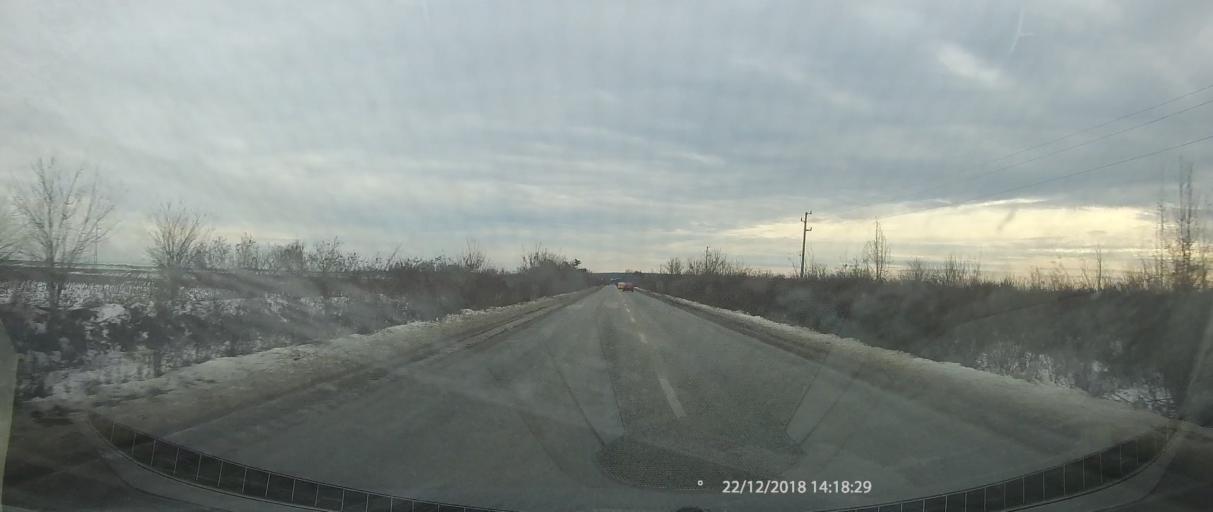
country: BG
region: Pleven
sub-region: Obshtina Pleven
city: Pleven
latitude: 43.4227
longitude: 24.7178
